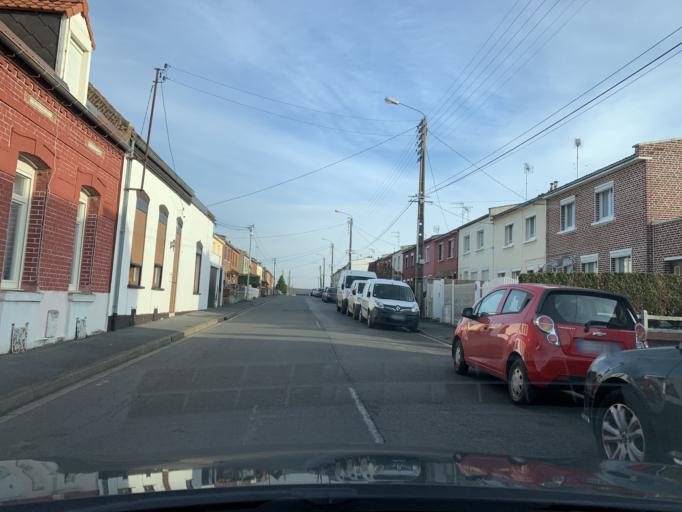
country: FR
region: Nord-Pas-de-Calais
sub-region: Departement du Nord
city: Cambrai
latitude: 50.1595
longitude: 3.2377
